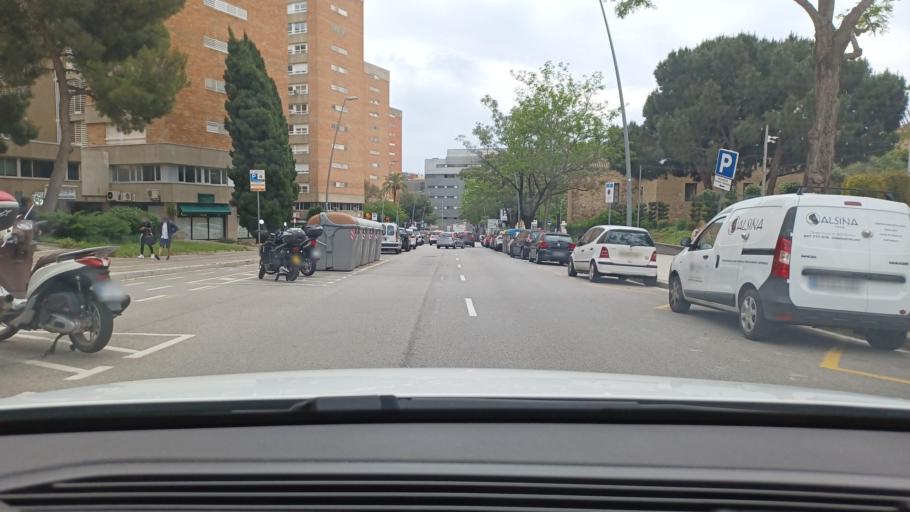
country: ES
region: Catalonia
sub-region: Provincia de Barcelona
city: les Corts
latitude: 41.3866
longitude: 2.1234
